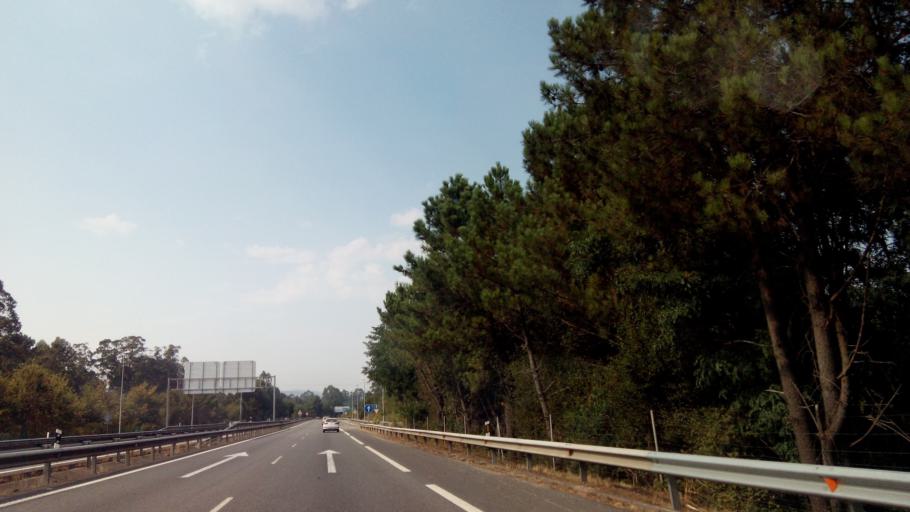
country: ES
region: Galicia
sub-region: Provincia de Pontevedra
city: Porrino
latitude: 42.1496
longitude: -8.6256
